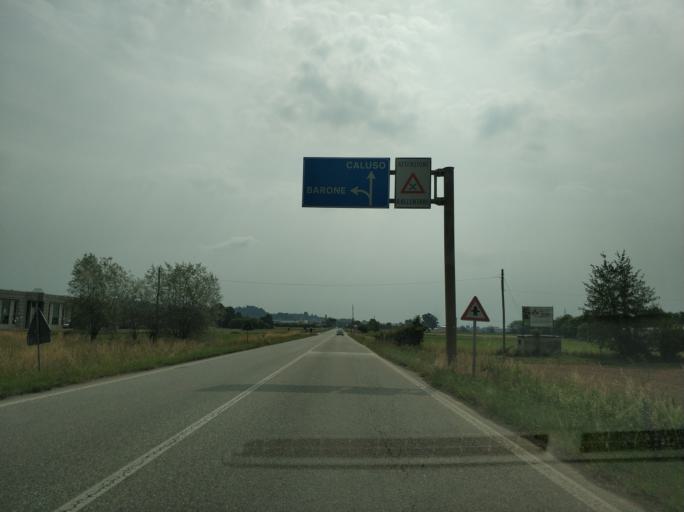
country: IT
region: Piedmont
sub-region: Provincia di Torino
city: Barone Canavese
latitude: 45.3080
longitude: 7.8630
